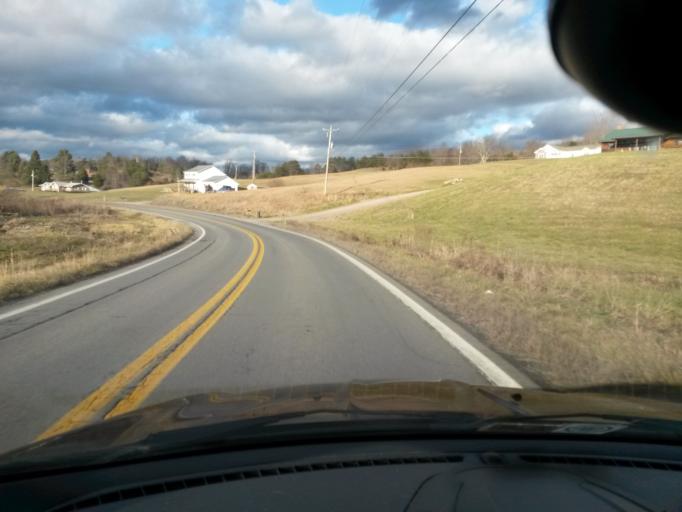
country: US
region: Virginia
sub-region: Giles County
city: Pembroke
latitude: 37.4708
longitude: -80.6571
